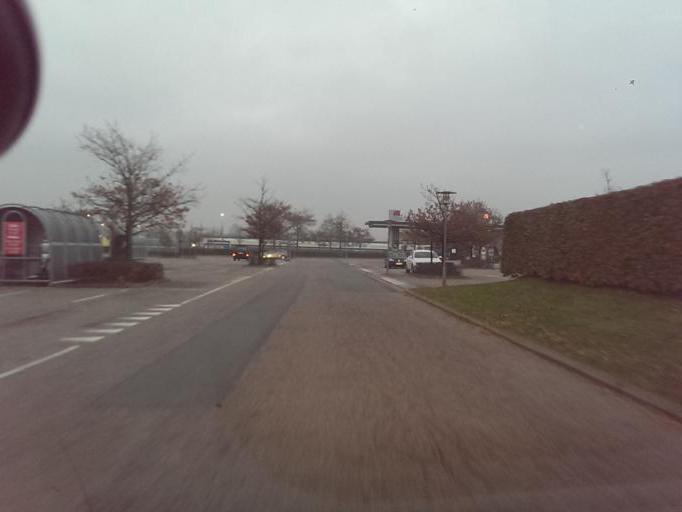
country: DK
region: South Denmark
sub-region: Esbjerg Kommune
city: Esbjerg
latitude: 55.5074
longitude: 8.4490
